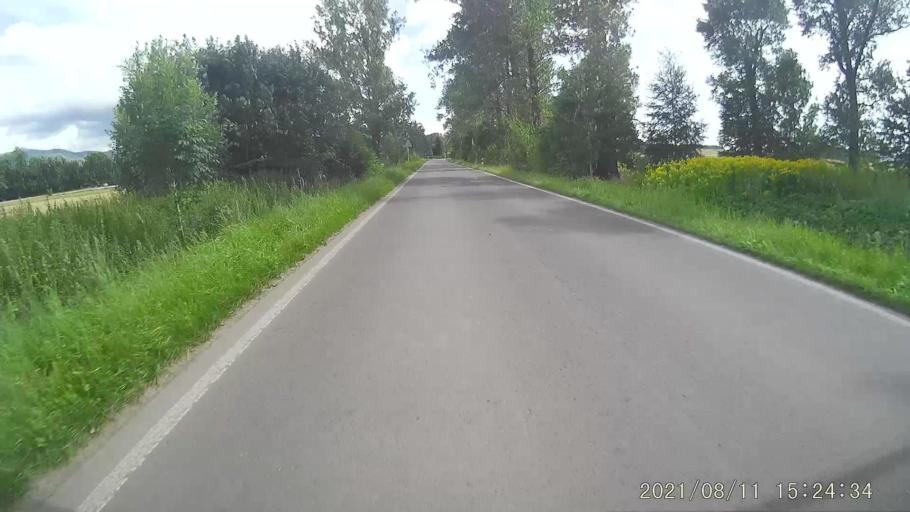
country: PL
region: Lower Silesian Voivodeship
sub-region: Powiat klodzki
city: Bystrzyca Klodzka
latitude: 50.2805
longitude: 16.6831
